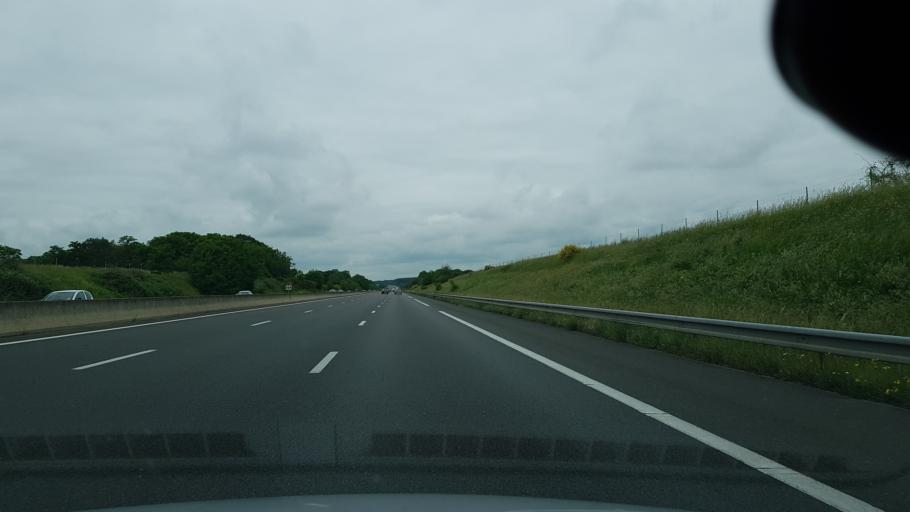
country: FR
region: Centre
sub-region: Departement du Loir-et-Cher
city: Saint-Sulpice-de-Pommeray
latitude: 47.6170
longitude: 1.2814
